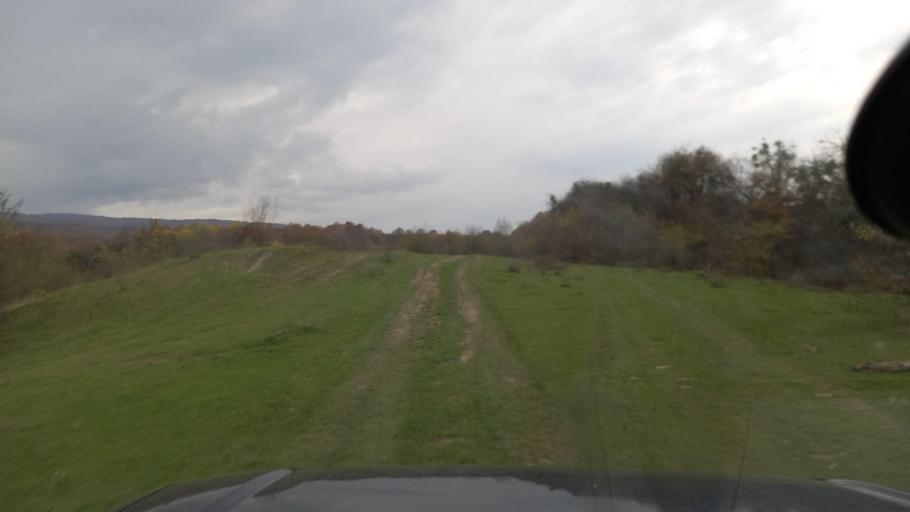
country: RU
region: Krasnodarskiy
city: Gubskaya
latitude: 44.2873
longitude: 40.5349
